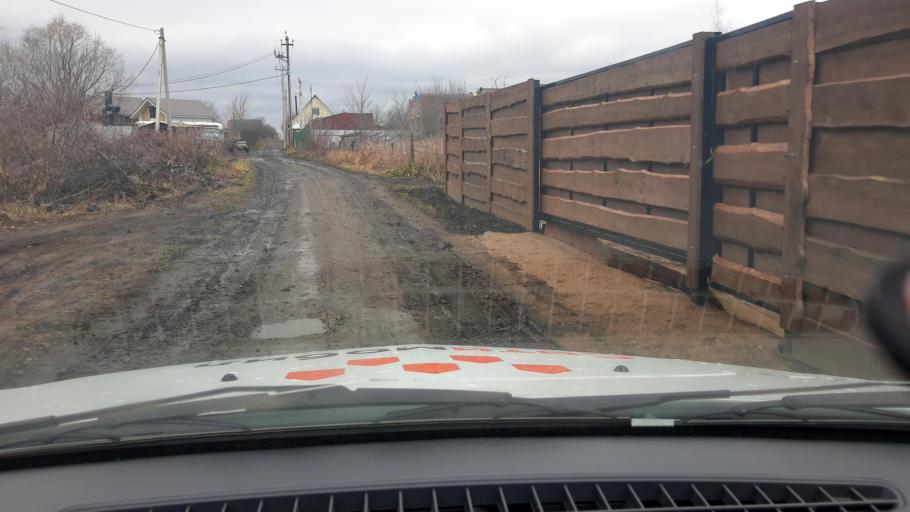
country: RU
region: Bashkortostan
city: Kabakovo
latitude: 54.7105
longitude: 56.1756
